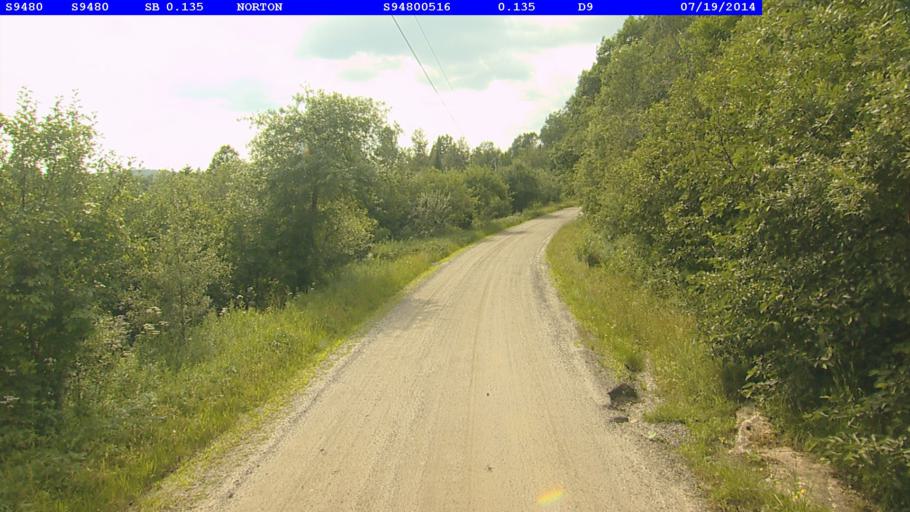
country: CA
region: Quebec
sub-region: Estrie
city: Coaticook
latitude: 44.9947
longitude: -71.7150
